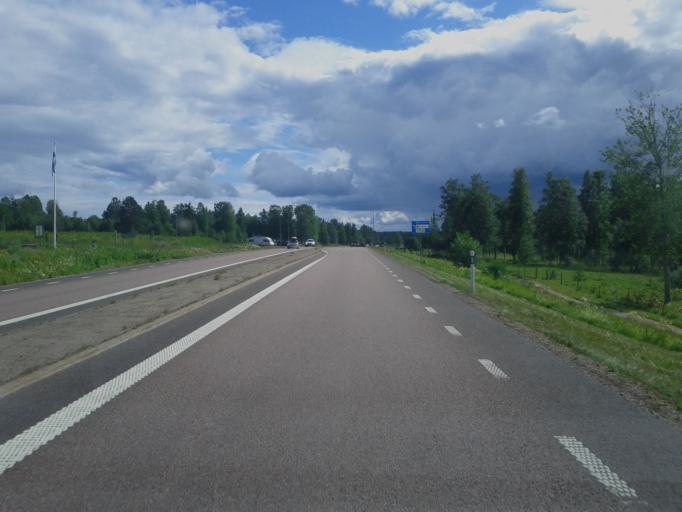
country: SE
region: Dalarna
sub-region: Rattviks Kommun
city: Raettvik
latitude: 60.8617
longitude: 15.1016
